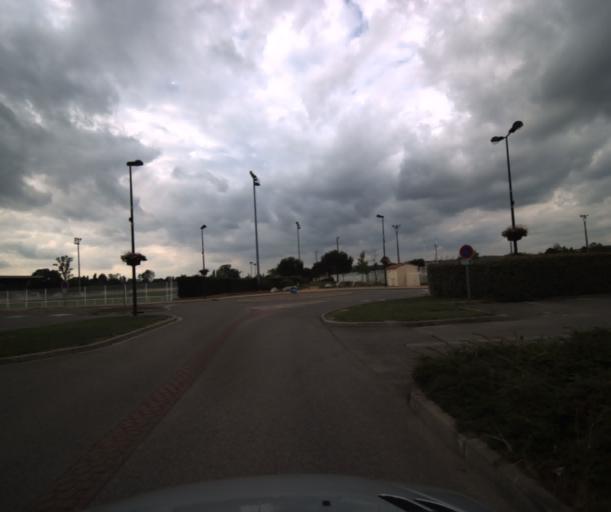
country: FR
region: Midi-Pyrenees
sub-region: Departement de la Haute-Garonne
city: Labarthe-sur-Leze
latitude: 43.4533
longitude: 1.3990
